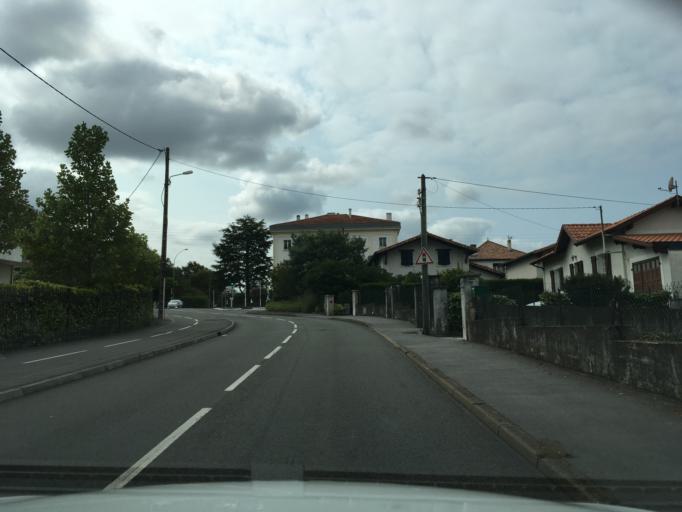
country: FR
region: Aquitaine
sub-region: Departement des Pyrenees-Atlantiques
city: Anglet
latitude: 43.4913
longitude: -1.5116
